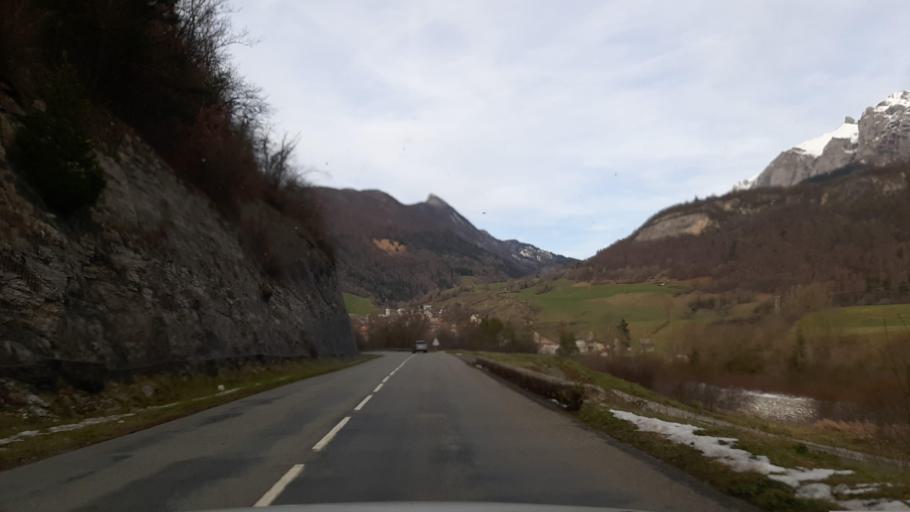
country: FR
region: Rhone-Alpes
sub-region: Departement de la Savoie
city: Gresy-sur-Isere
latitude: 45.6590
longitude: 6.1628
